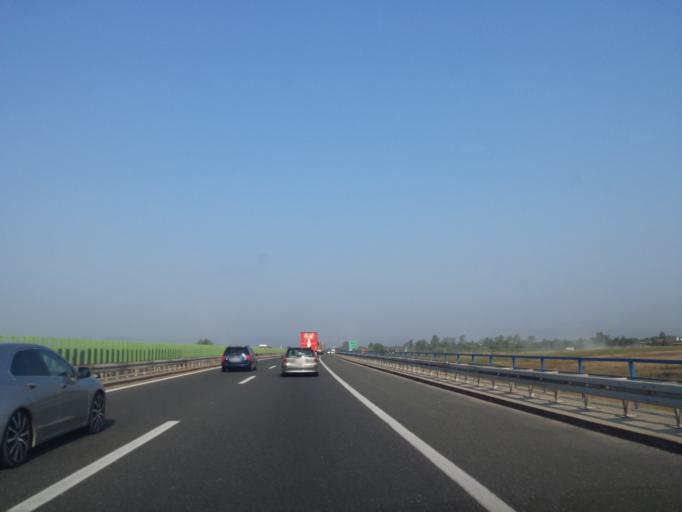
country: HR
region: Grad Zagreb
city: Zadvorsko
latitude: 45.7488
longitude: 15.9199
